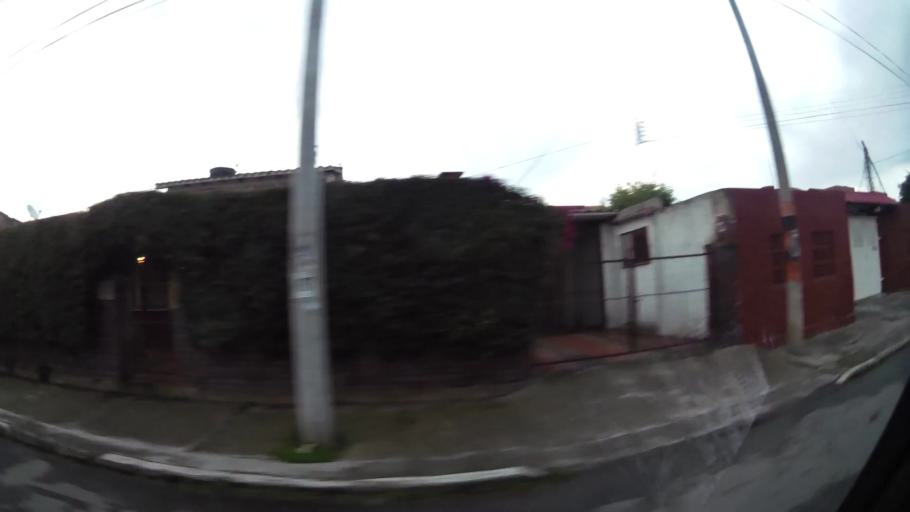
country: CO
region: Cundinamarca
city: Chia
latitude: 4.8470
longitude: -74.0585
